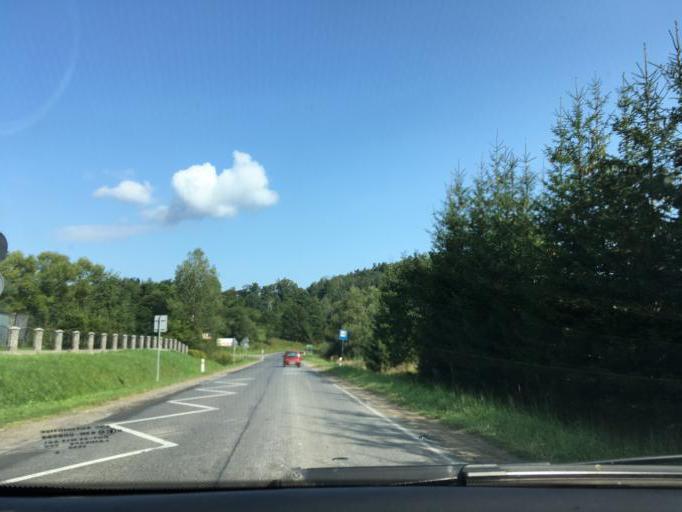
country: PL
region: Subcarpathian Voivodeship
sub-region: Powiat bieszczadzki
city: Czarna
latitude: 49.3847
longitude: 22.6365
